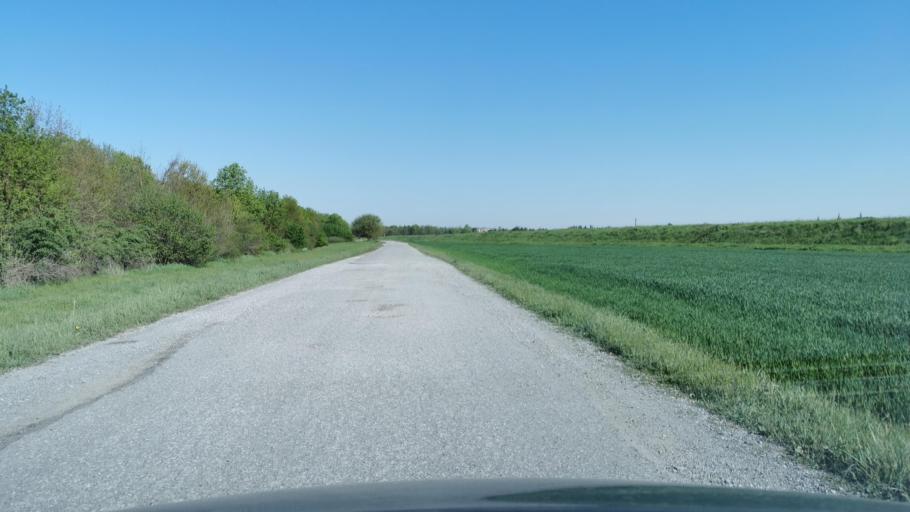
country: IT
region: Lombardy
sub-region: Provincia di Cremona
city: Bosco Ex Parmigiano
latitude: 45.1131
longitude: 10.0169
